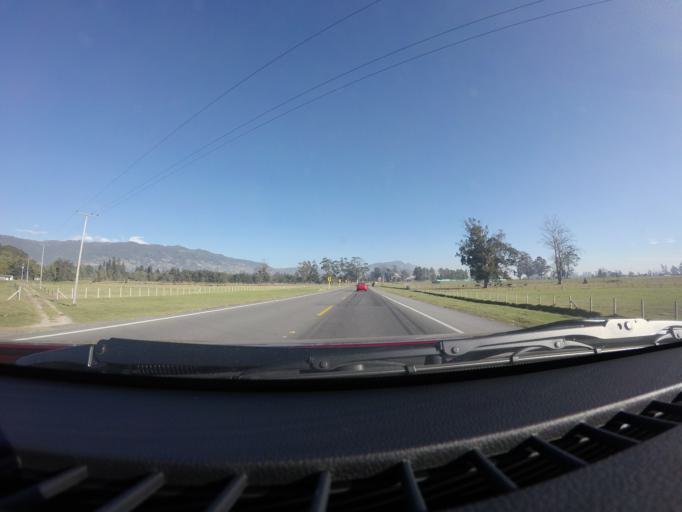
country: CO
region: Cundinamarca
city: Cogua
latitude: 5.0371
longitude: -73.9719
